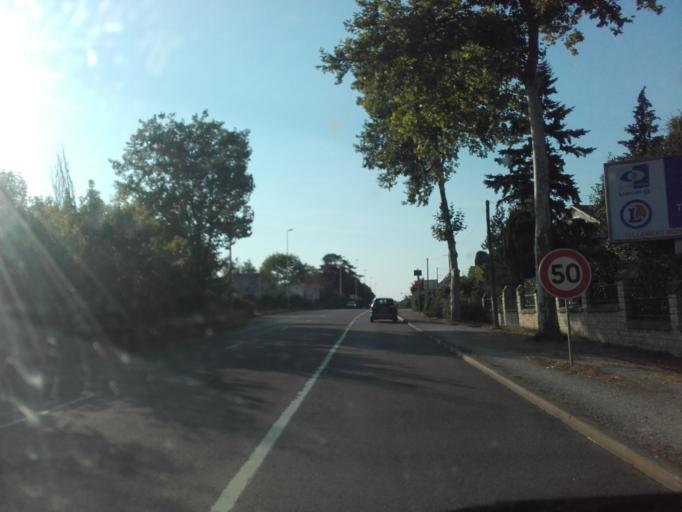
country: FR
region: Bourgogne
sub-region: Departement de l'Yonne
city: Auxerre
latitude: 47.7912
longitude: 3.5900
